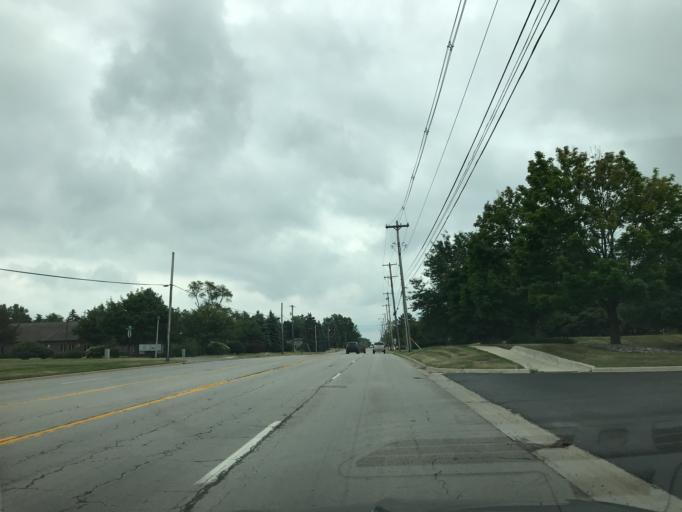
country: US
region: Michigan
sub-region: Eaton County
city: Waverly
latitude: 42.7388
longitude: -84.6621
